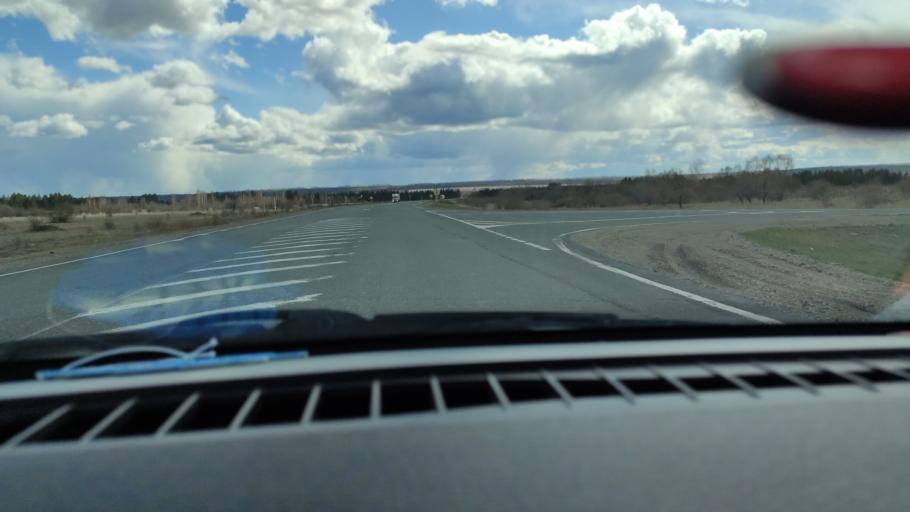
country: RU
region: Samara
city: Varlamovo
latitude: 53.1537
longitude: 48.2843
